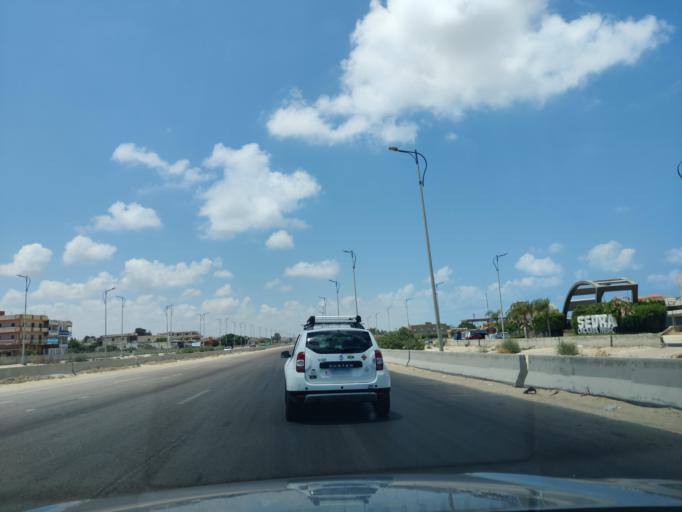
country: EG
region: Alexandria
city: Alexandria
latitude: 31.0042
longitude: 29.6163
